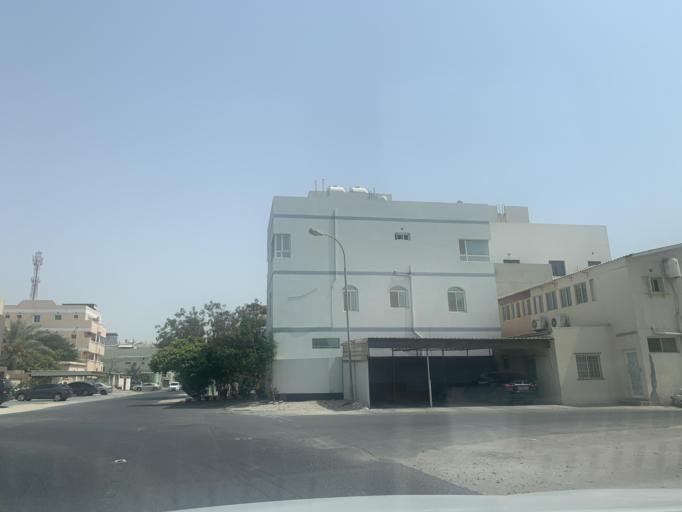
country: BH
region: Manama
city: Jidd Hafs
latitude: 26.2247
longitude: 50.4664
